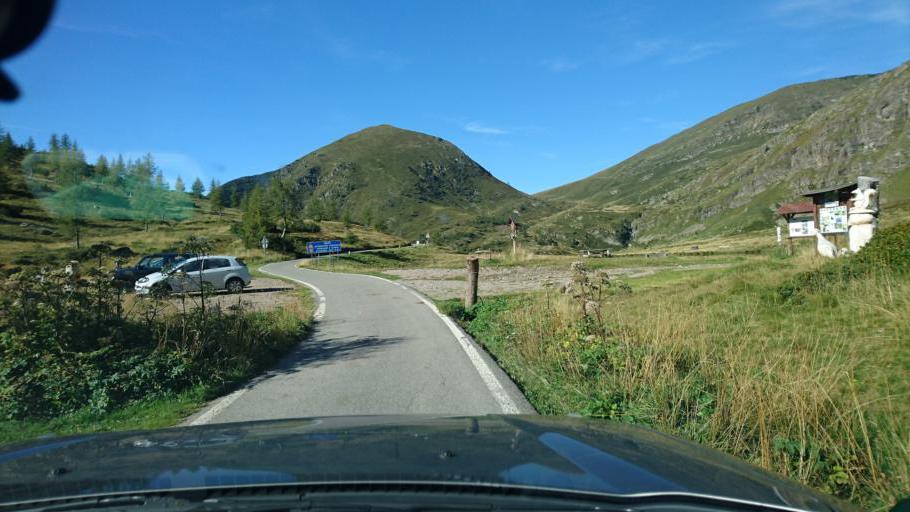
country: IT
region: Lombardy
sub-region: Provincia di Bergamo
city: Schilpario
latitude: 46.0366
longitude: 10.1994
